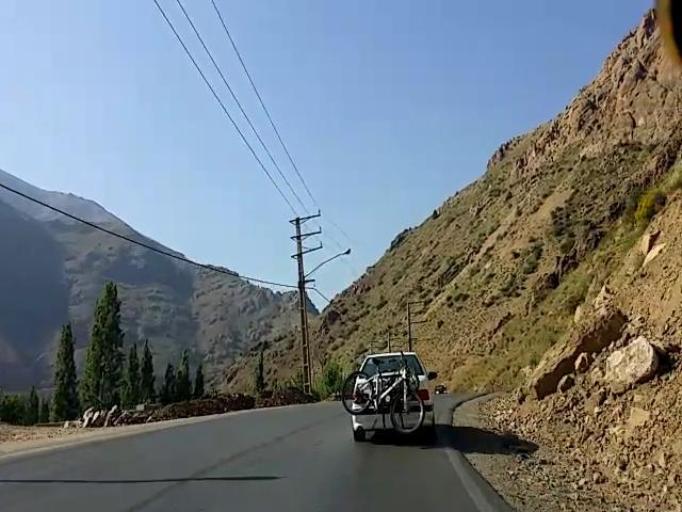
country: IR
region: Tehran
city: Tajrish
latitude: 36.0666
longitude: 51.3103
